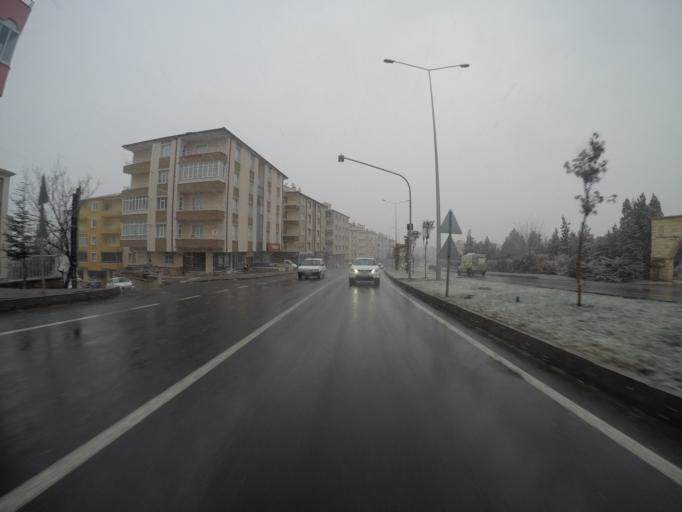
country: TR
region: Nevsehir
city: Nevsehir
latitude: 38.6339
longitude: 34.7294
